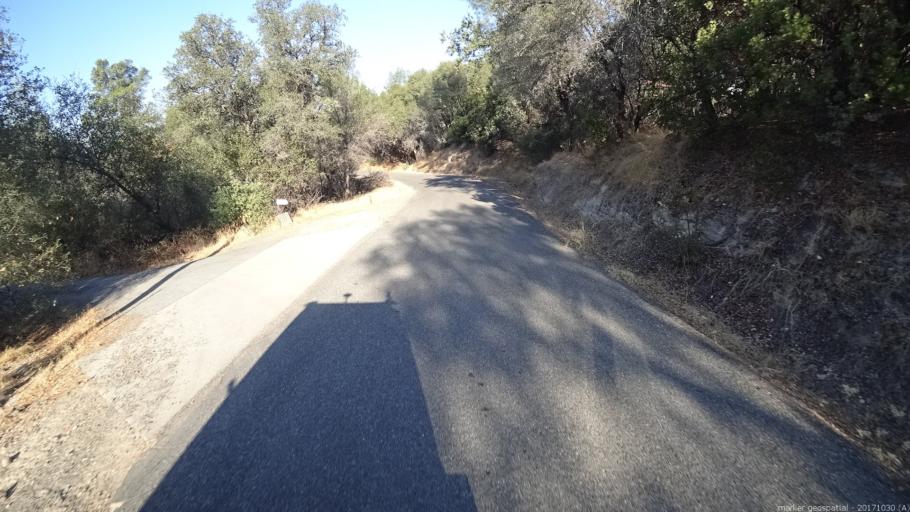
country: US
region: California
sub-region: Shasta County
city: Palo Cedro
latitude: 40.5667
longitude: -122.1372
